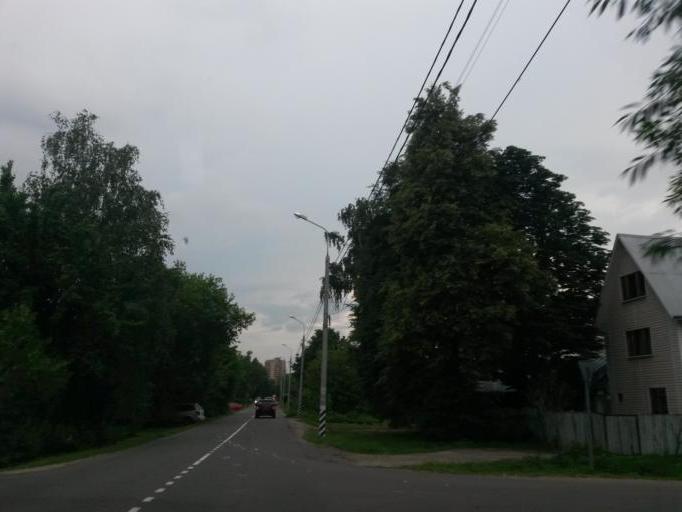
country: RU
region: Moskovskaya
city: Domodedovo
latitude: 55.4463
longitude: 37.7551
